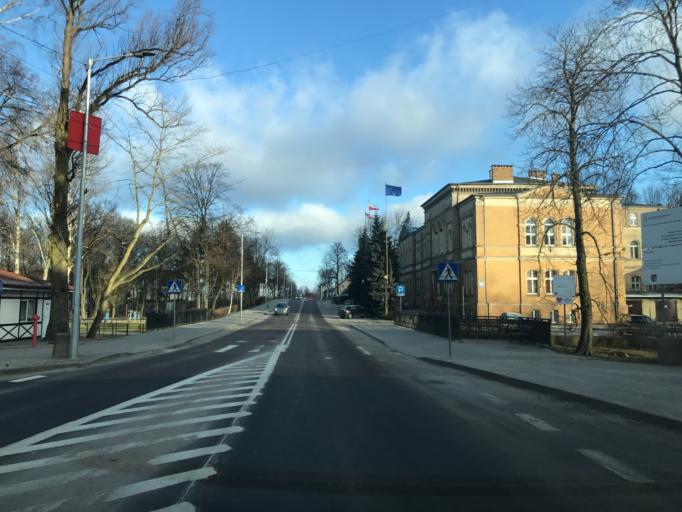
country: PL
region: Warmian-Masurian Voivodeship
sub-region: Powiat ostrodzki
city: Ostroda
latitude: 53.7037
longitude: 19.9604
